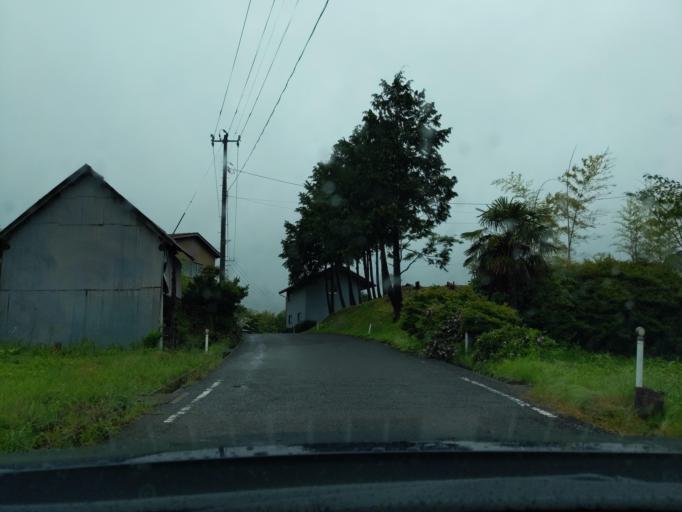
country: JP
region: Fukushima
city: Motomiya
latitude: 37.5015
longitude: 140.4523
